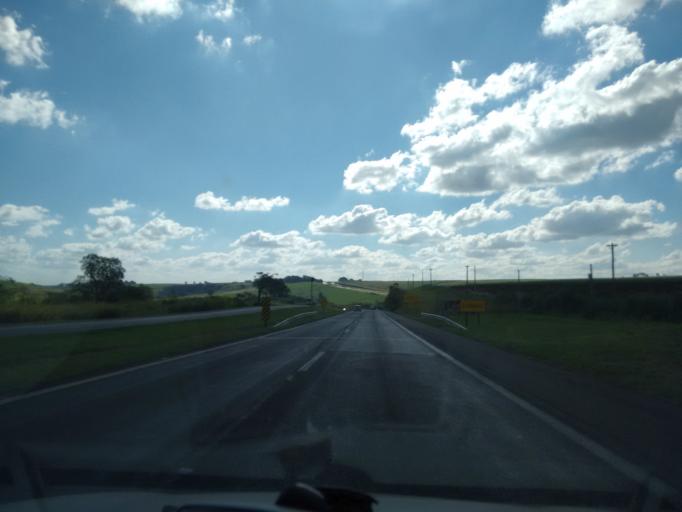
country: BR
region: Sao Paulo
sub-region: Ibate
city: Ibate
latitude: -21.8838
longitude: -48.0851
